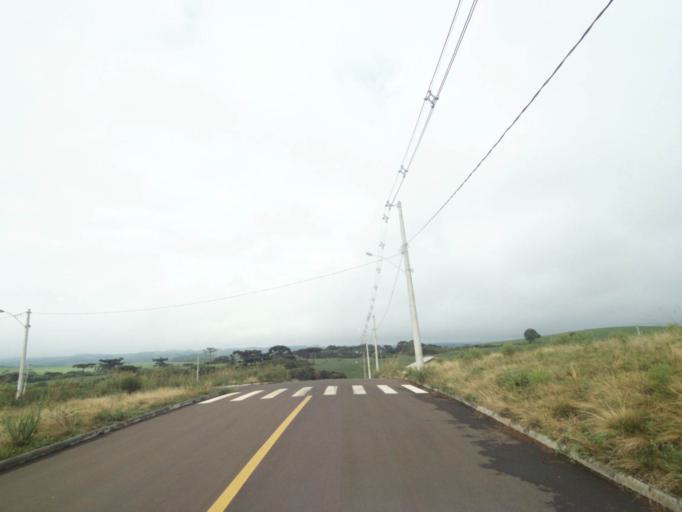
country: BR
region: Rio Grande do Sul
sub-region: Lagoa Vermelha
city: Lagoa Vermelha
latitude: -28.2282
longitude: -51.5211
